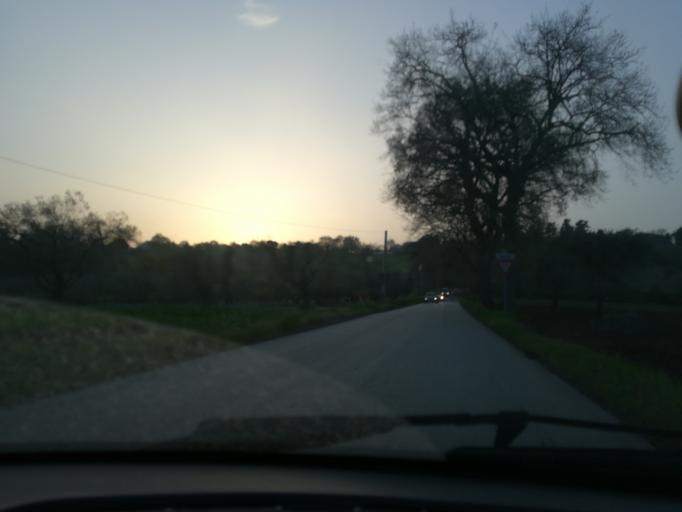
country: IT
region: The Marches
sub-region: Provincia di Macerata
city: Macerata
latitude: 43.2773
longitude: 13.4511
